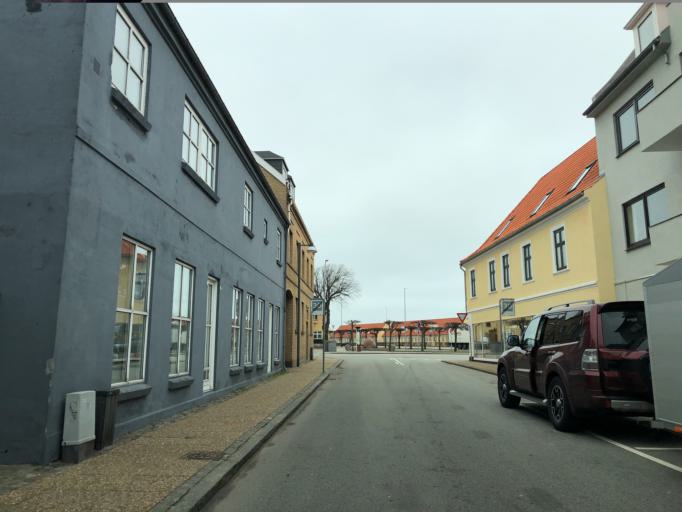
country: DK
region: North Denmark
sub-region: Frederikshavn Kommune
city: Frederikshavn
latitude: 57.4452
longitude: 10.5393
